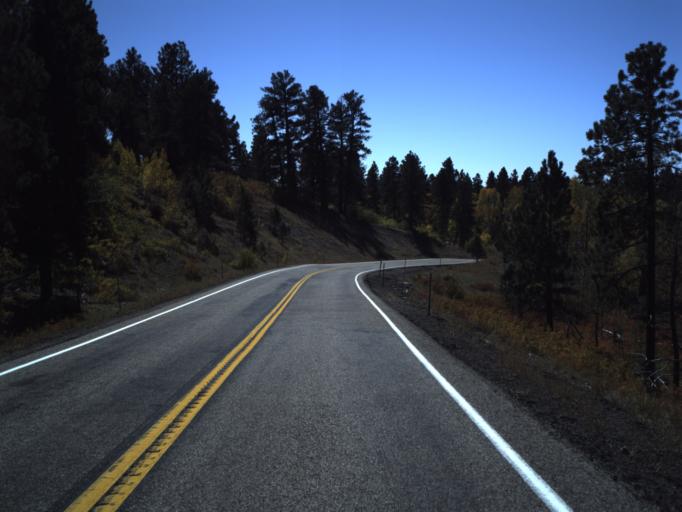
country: US
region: Utah
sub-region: Wayne County
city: Loa
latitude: 38.0063
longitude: -111.4052
